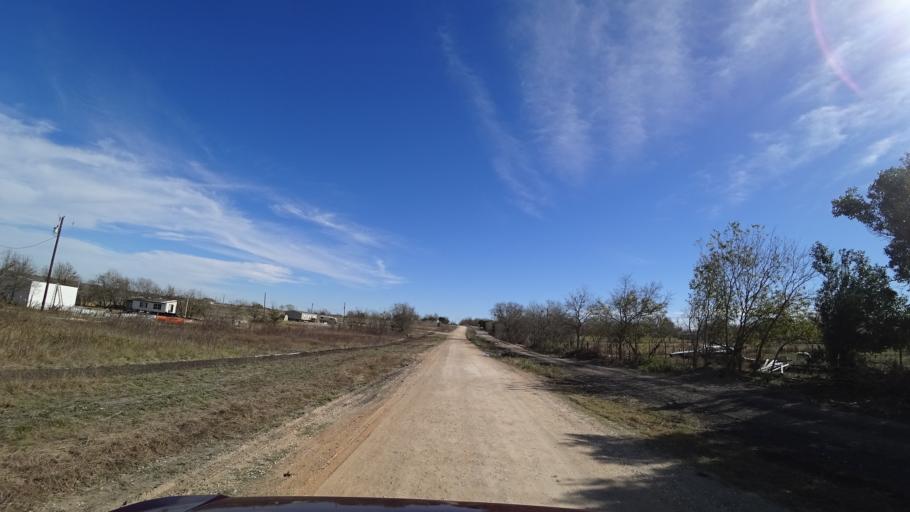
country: US
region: Texas
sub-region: Travis County
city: Onion Creek
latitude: 30.1073
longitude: -97.7212
